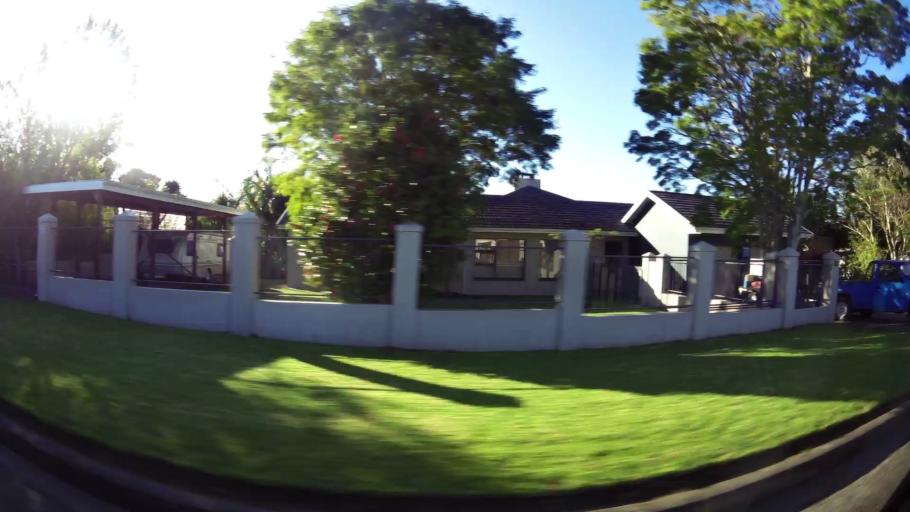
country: ZA
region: Western Cape
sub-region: Eden District Municipality
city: George
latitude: -33.9421
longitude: 22.4571
